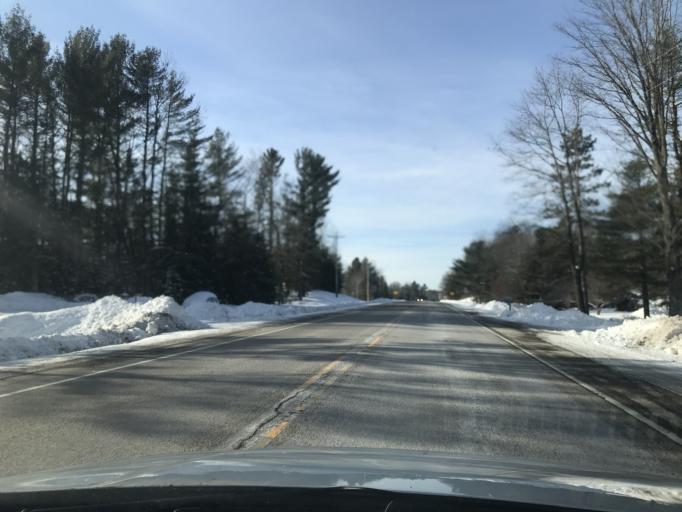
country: US
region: Wisconsin
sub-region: Oconto County
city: Gillett
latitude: 45.1291
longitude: -88.4195
